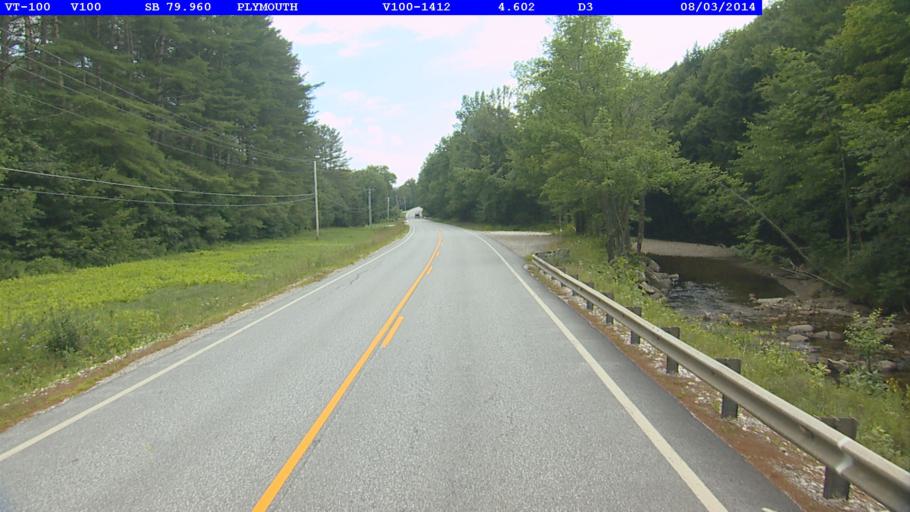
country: US
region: Vermont
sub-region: Windsor County
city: Woodstock
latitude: 43.5209
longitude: -72.7332
